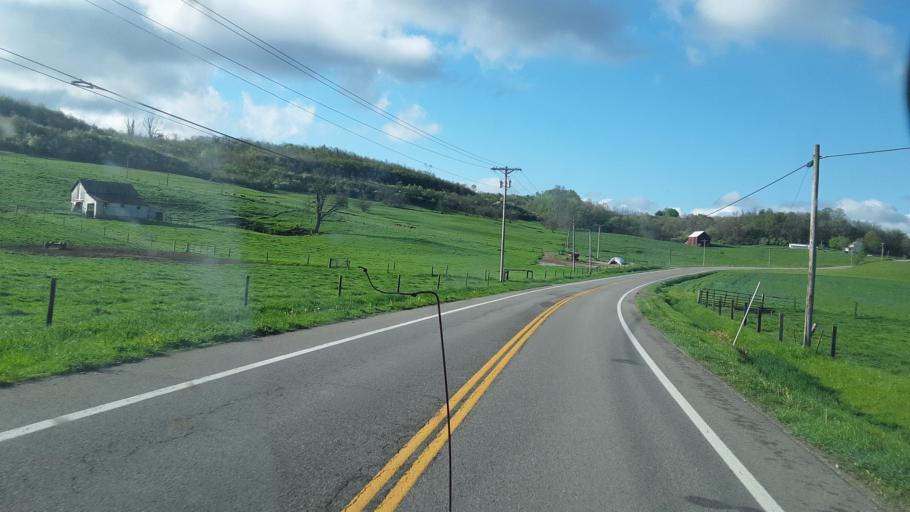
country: US
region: Ohio
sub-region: Muskingum County
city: New Concord
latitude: 39.8885
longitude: -81.6701
